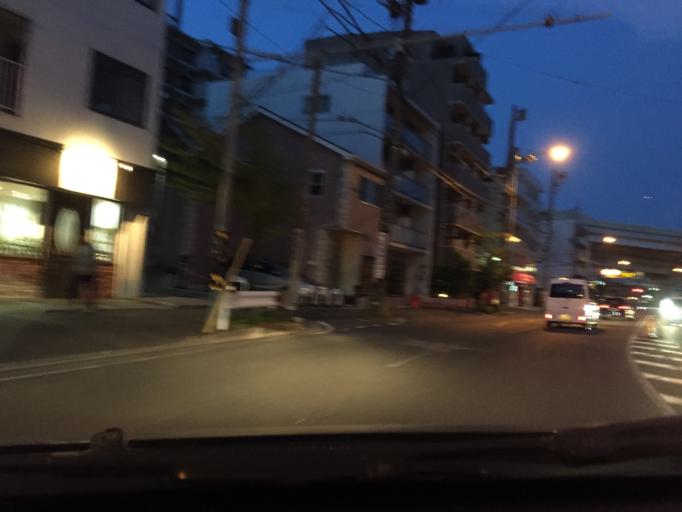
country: JP
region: Kanagawa
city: Yokohama
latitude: 35.4356
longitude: 139.6105
